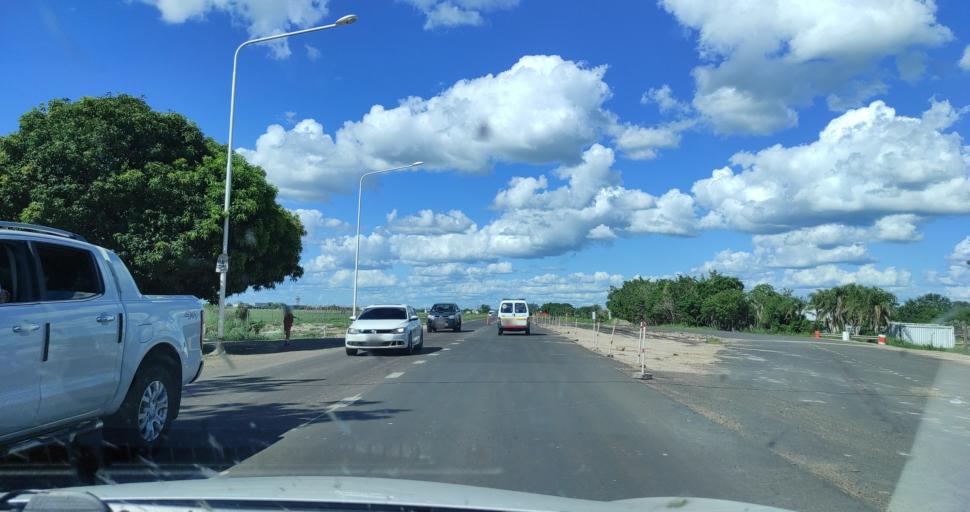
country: AR
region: Corrientes
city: Corrientes
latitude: -27.4590
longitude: -58.7659
